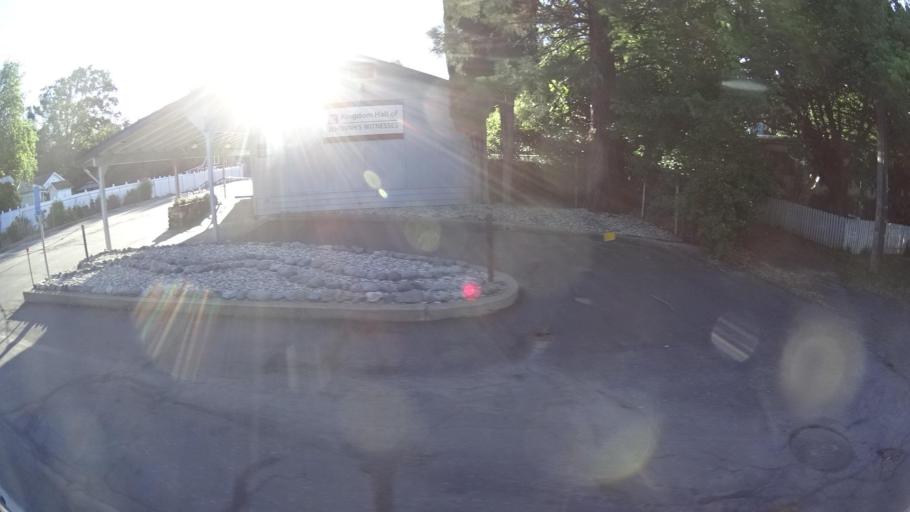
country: US
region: California
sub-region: Lake County
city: Upper Lake
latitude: 39.1663
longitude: -122.9104
